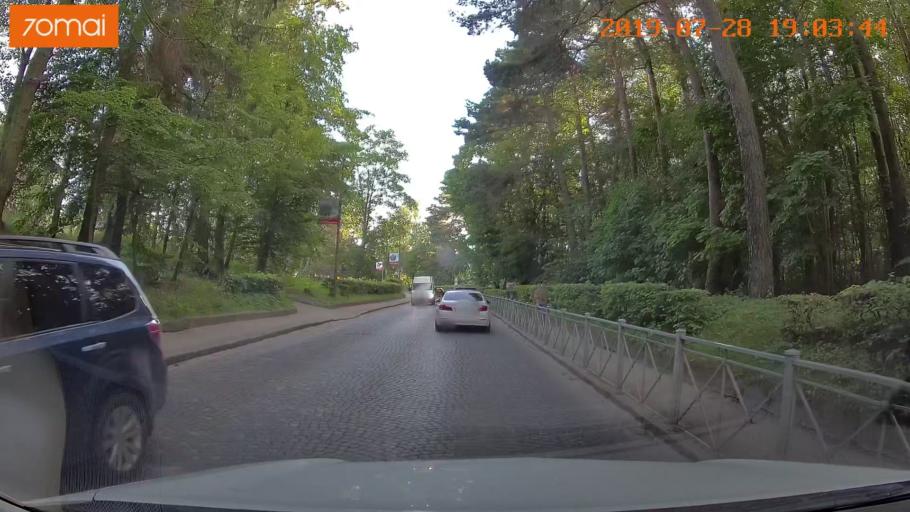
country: RU
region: Kaliningrad
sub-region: Gorod Svetlogorsk
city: Svetlogorsk
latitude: 54.9350
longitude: 20.1615
